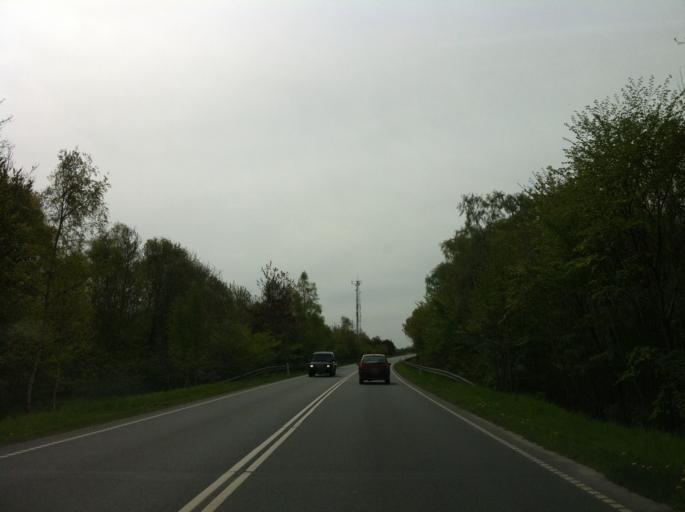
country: DK
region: Capital Region
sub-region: Egedal Kommune
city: Olstykke
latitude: 55.7986
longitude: 12.1651
